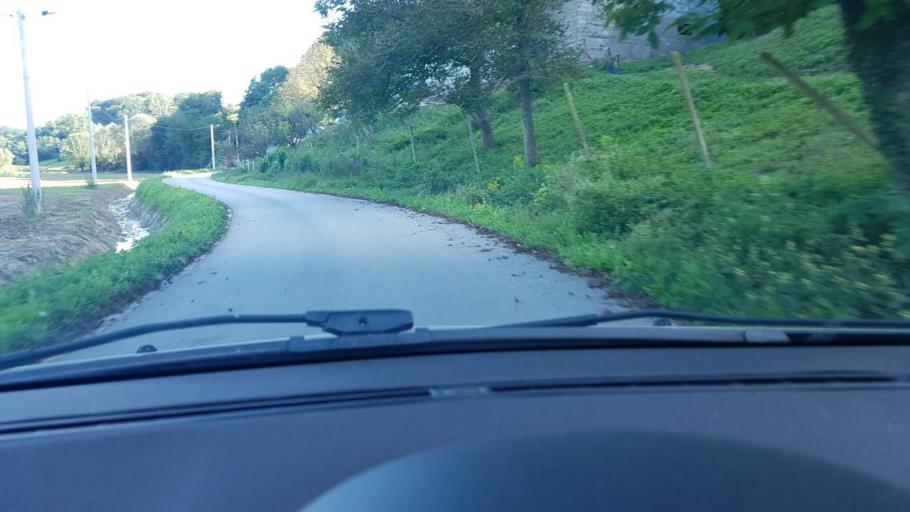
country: HR
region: Krapinsko-Zagorska
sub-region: Grad Krapina
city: Krapina
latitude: 46.1395
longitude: 15.8356
